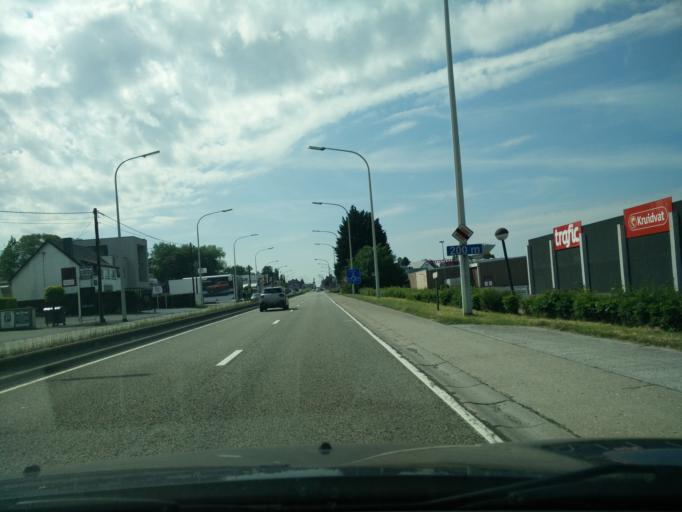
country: BE
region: Wallonia
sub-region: Province du Hainaut
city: Gerpinnes
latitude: 50.3460
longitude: 4.4727
